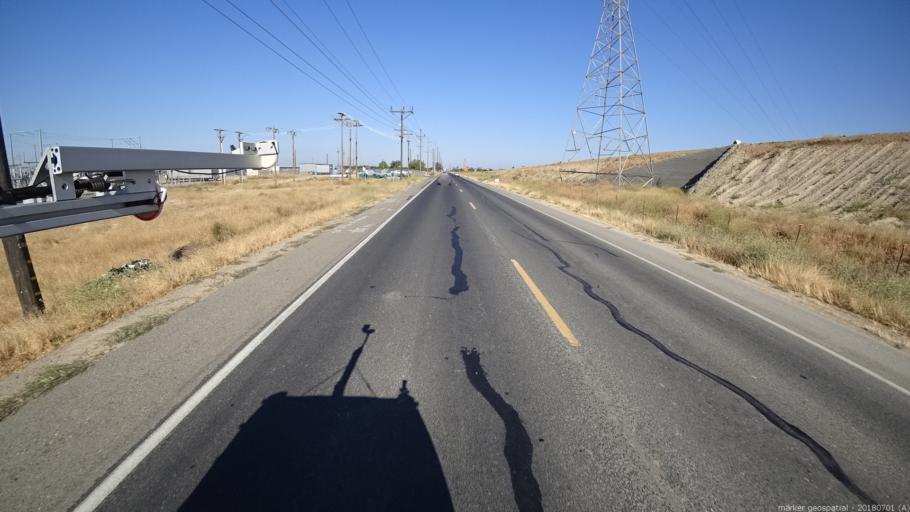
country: US
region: California
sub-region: Madera County
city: Parksdale
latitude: 36.9233
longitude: -119.9835
